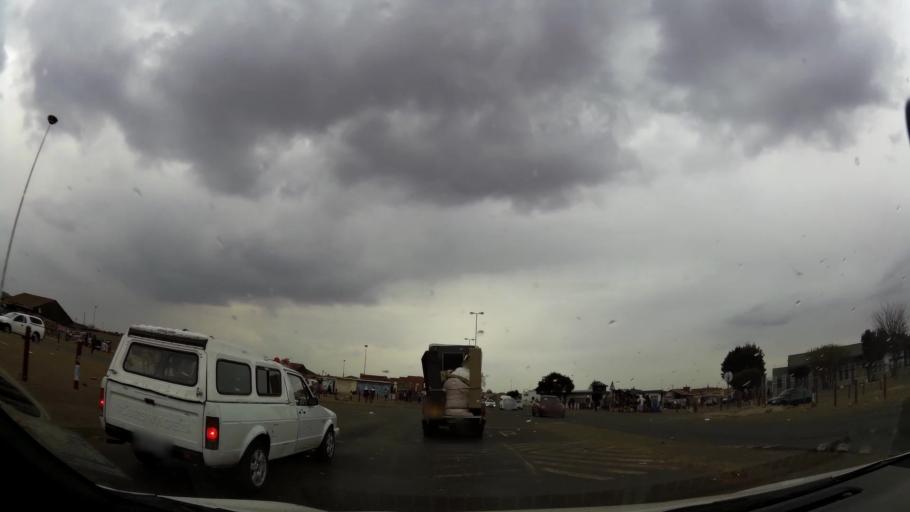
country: ZA
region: Gauteng
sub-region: Ekurhuleni Metropolitan Municipality
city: Germiston
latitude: -26.3488
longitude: 28.1498
